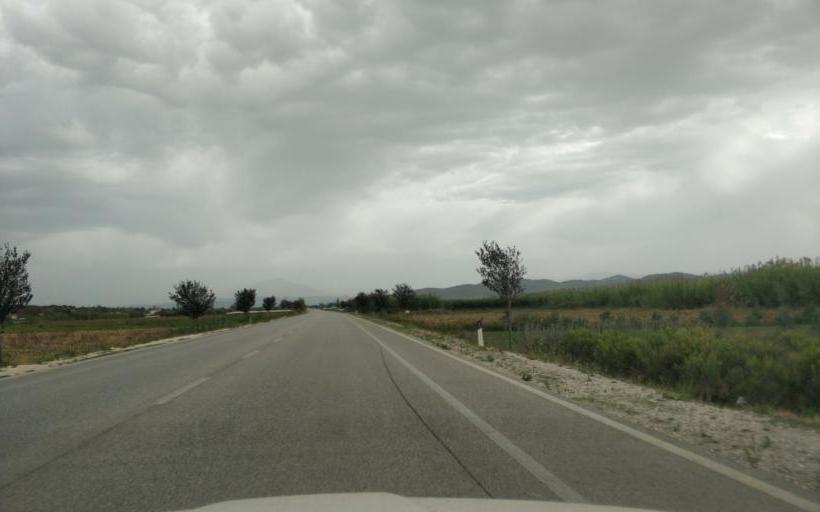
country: AL
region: Fier
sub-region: Rrethi i Fierit
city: Frakulla e Madhe
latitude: 40.6368
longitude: 19.5041
